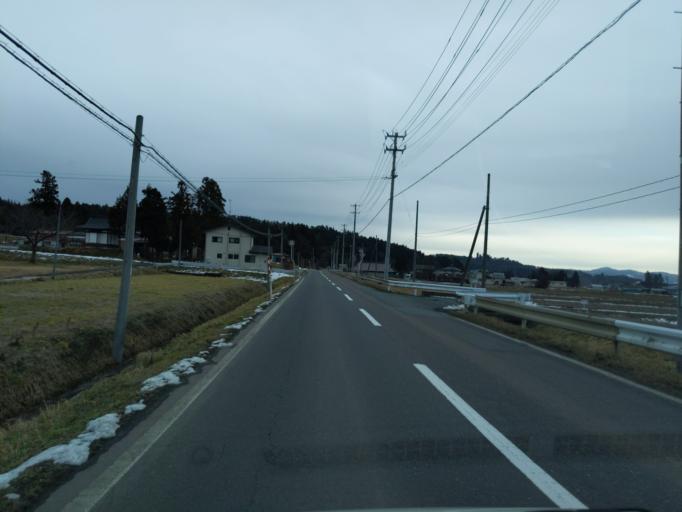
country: JP
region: Iwate
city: Mizusawa
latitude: 39.1732
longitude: 141.1929
